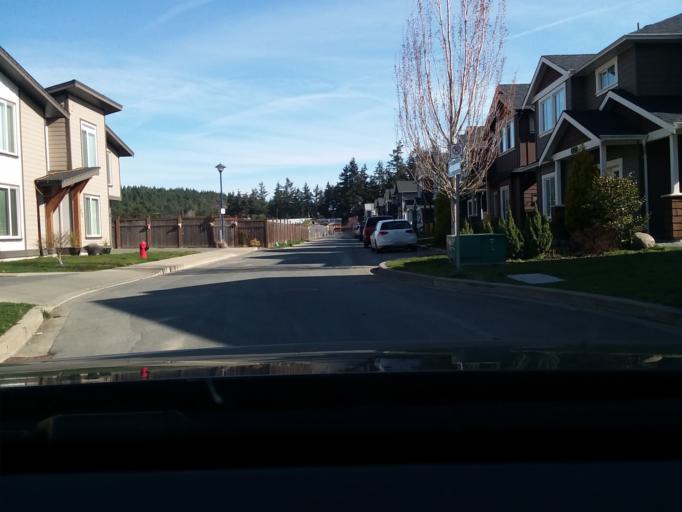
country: CA
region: British Columbia
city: Langford
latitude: 48.4265
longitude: -123.5344
